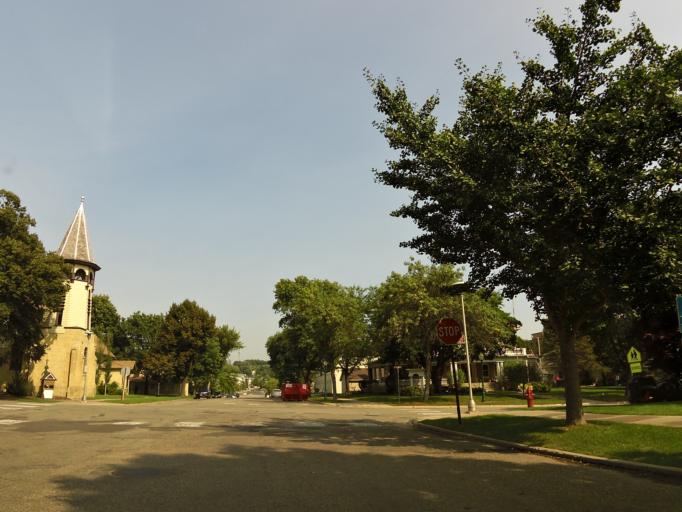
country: US
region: Minnesota
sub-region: Carver County
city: Chaska
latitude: 44.7873
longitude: -93.5996
